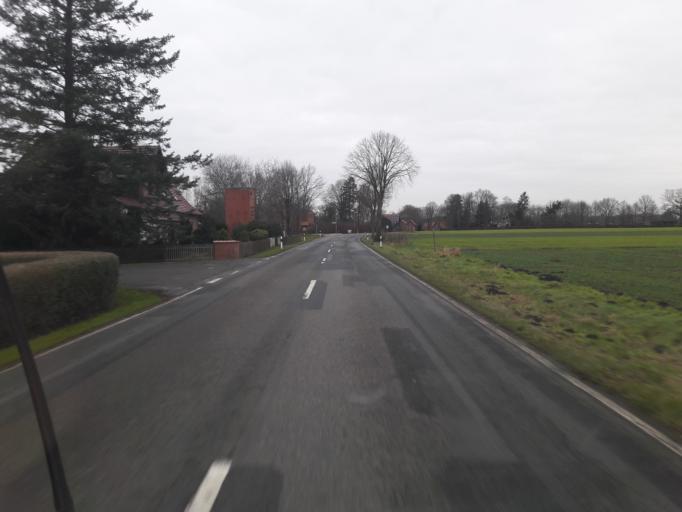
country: DE
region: Lower Saxony
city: Warmsen
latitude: 52.4210
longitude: 8.8564
